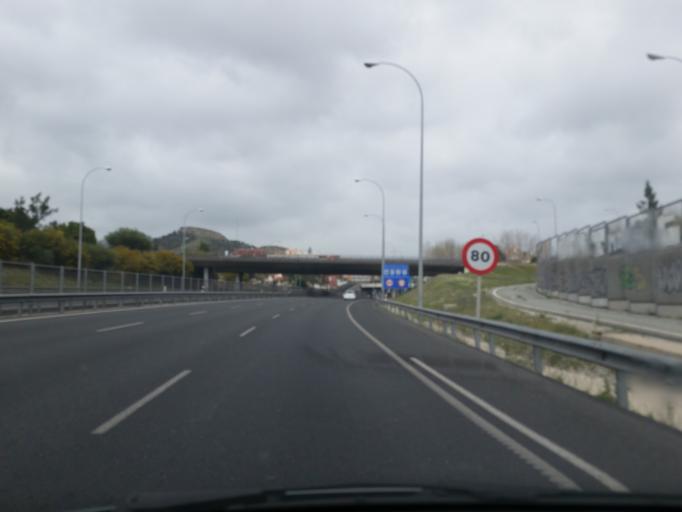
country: ES
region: Andalusia
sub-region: Provincia de Malaga
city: Malaga
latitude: 36.7184
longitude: -4.4578
